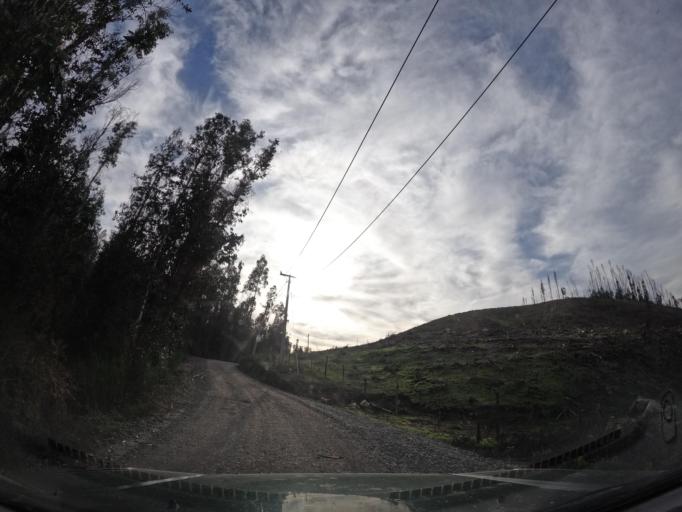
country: CL
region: Biobio
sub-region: Provincia de Concepcion
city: Chiguayante
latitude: -37.0172
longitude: -72.9083
